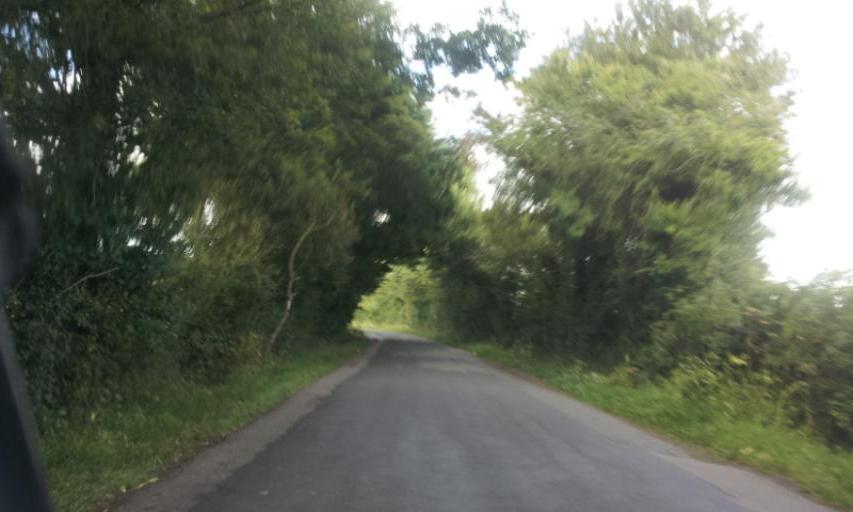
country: GB
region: England
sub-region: Kent
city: Headcorn
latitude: 51.1810
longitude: 0.6281
